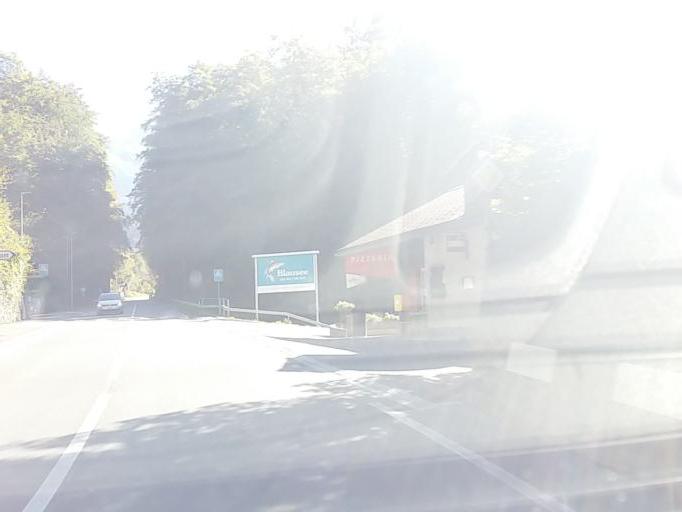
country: CH
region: Bern
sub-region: Frutigen-Niedersimmental District
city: Kandersteg
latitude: 46.5346
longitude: 7.6680
